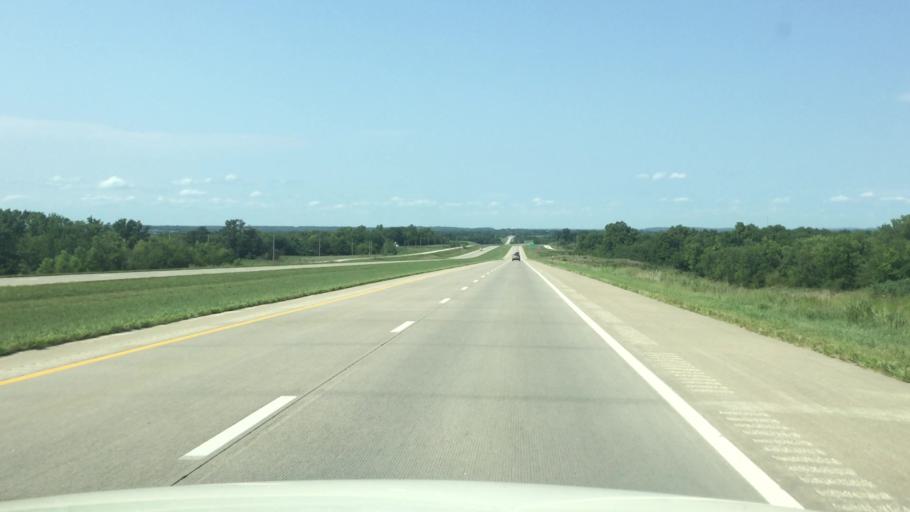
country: US
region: Kansas
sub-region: Linn County
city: Pleasanton
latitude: 38.1169
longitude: -94.7133
